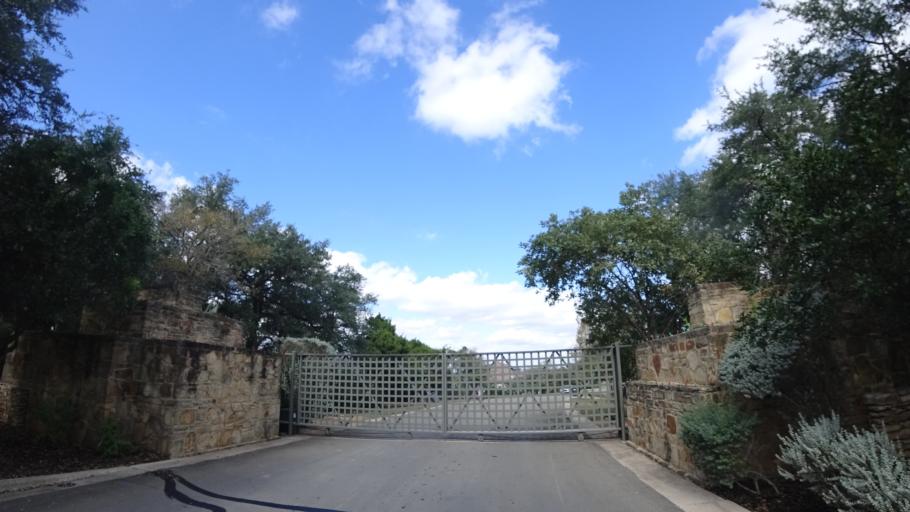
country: US
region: Texas
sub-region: Travis County
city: Barton Creek
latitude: 30.2581
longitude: -97.8708
